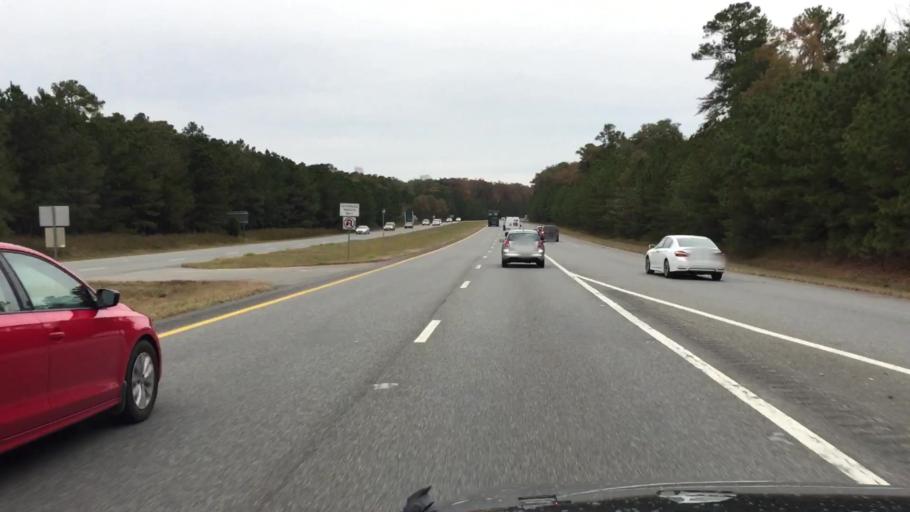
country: US
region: Virginia
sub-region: James City County
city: Williamsburg
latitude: 37.2762
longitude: -76.7526
